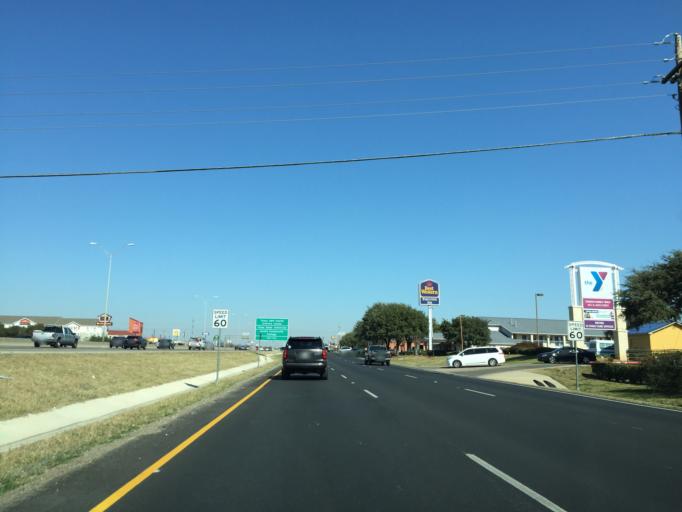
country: US
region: Texas
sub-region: Williamson County
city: Round Rock
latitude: 30.5250
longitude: -97.6896
